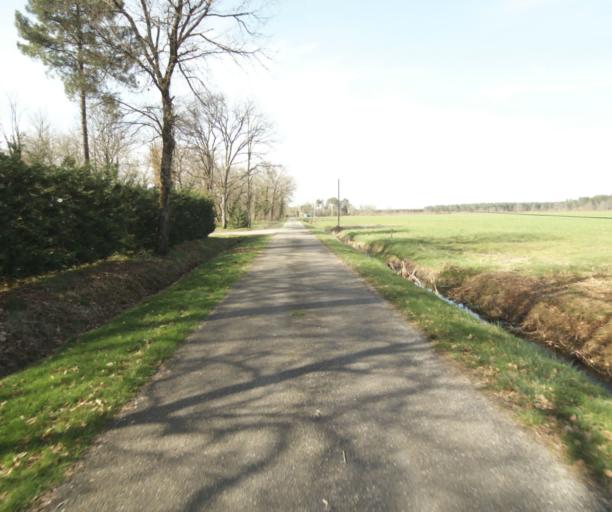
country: FR
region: Aquitaine
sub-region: Departement des Landes
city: Roquefort
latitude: 44.1580
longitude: -0.1995
